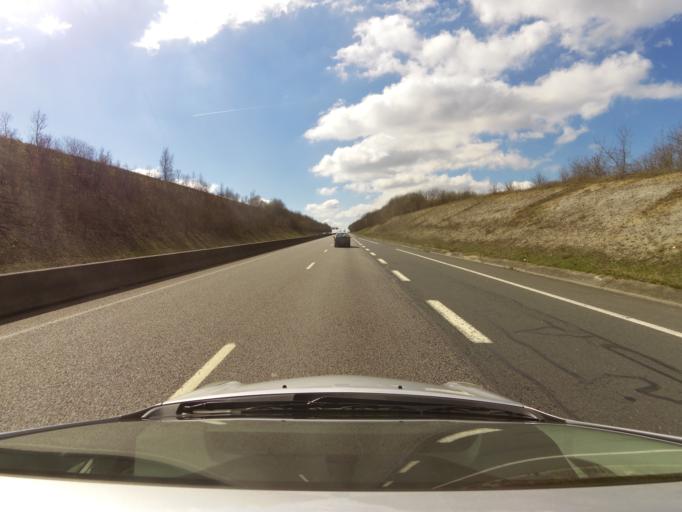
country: FR
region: Haute-Normandie
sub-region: Departement de la Seine-Maritime
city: Neufchatel-en-Bray
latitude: 49.7511
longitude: 1.4810
